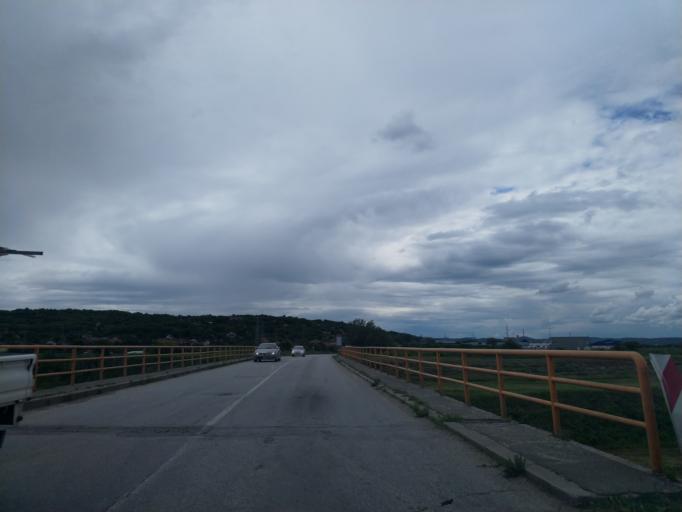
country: RS
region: Central Serbia
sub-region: Pomoravski Okrug
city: Jagodina
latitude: 43.9580
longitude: 21.2892
